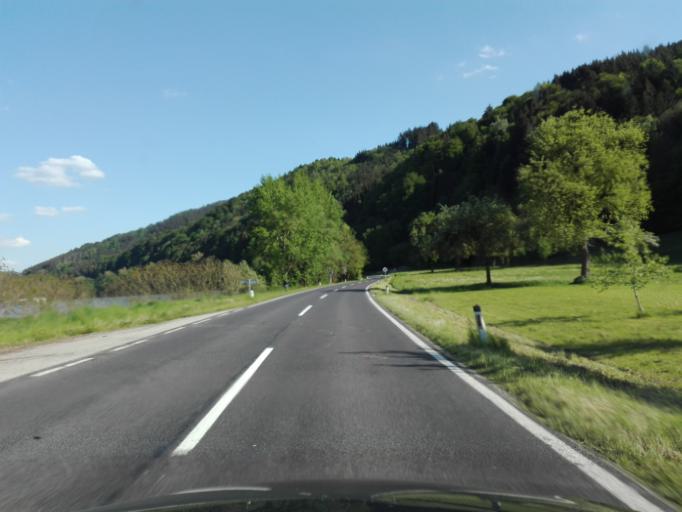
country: AT
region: Upper Austria
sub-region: Politischer Bezirk Rohrbach
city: Pfarrkirchen im Muehlkreis
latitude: 48.4710
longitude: 13.7739
